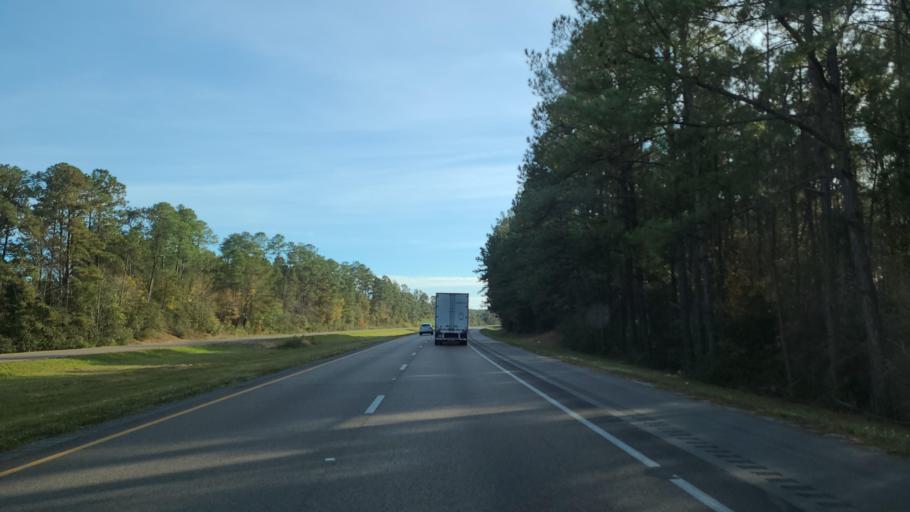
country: US
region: Mississippi
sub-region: Forrest County
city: Hattiesburg
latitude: 31.2345
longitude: -89.3226
